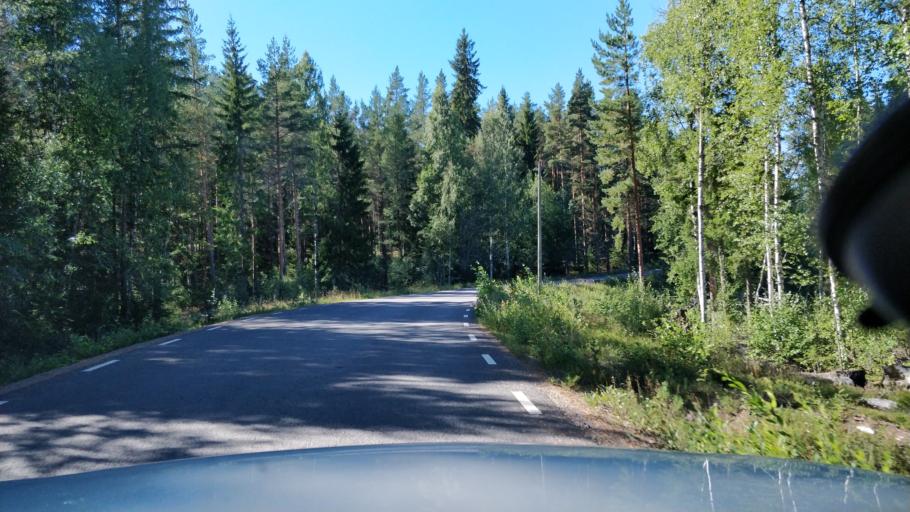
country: SE
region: Dalarna
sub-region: Faluns Kommun
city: Bjursas
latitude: 60.7491
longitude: 15.5278
